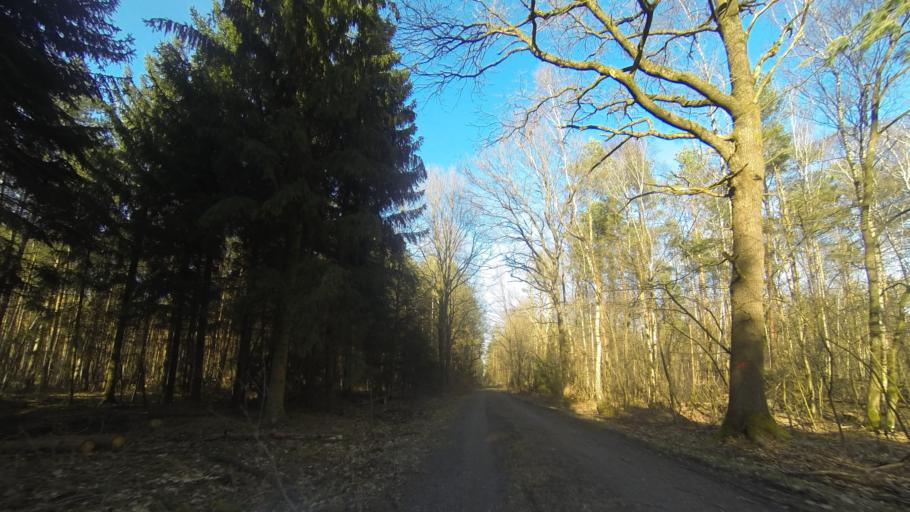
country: DE
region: Saxony
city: Laussnitz
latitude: 51.2689
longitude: 13.8535
